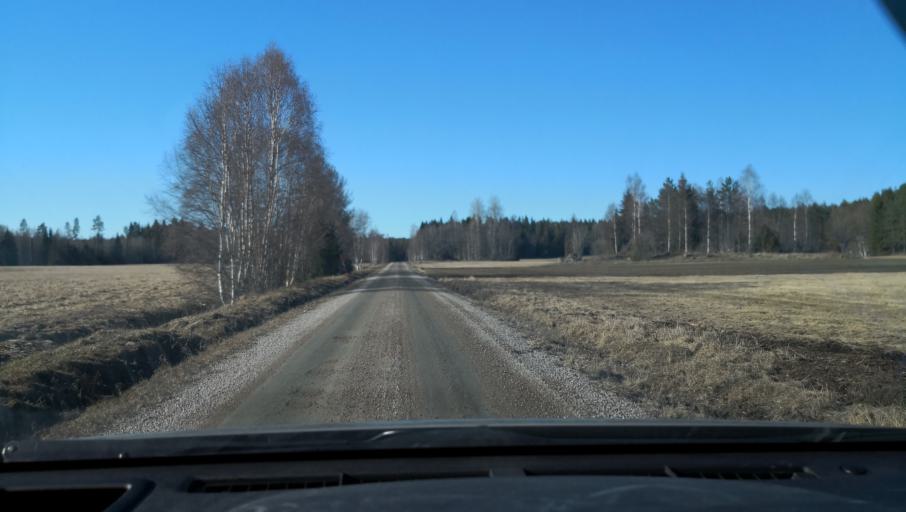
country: SE
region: Vaestmanland
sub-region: Sala Kommun
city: Sala
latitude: 60.1306
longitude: 16.6525
